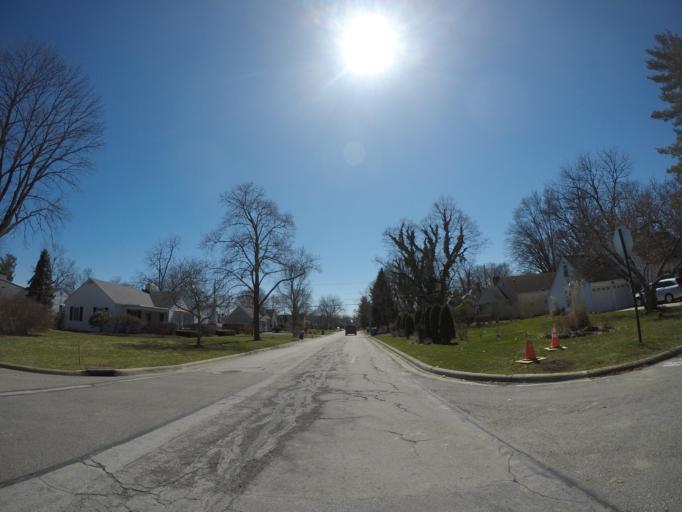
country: US
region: Ohio
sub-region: Franklin County
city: Upper Arlington
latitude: 40.0144
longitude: -83.0727
